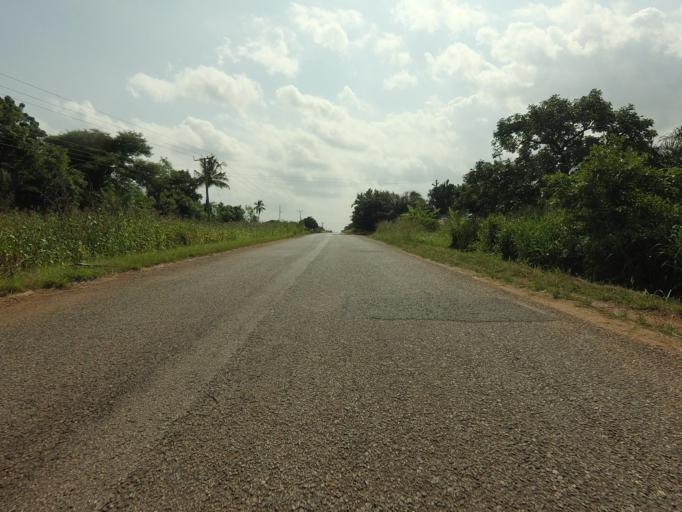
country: GH
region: Volta
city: Ho
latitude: 6.4069
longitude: 0.7734
